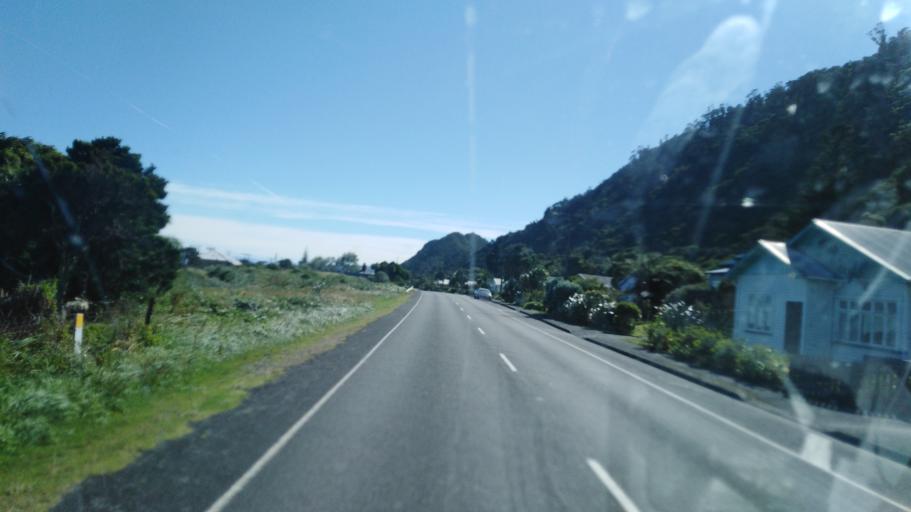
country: NZ
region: West Coast
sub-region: Buller District
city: Westport
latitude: -41.6381
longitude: 171.8467
